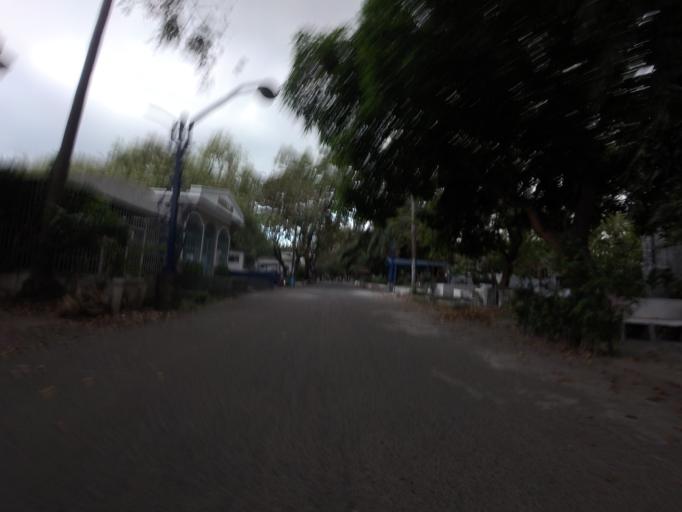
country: PH
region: Metro Manila
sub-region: Makati City
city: Makati City
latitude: 14.5654
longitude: 121.0201
